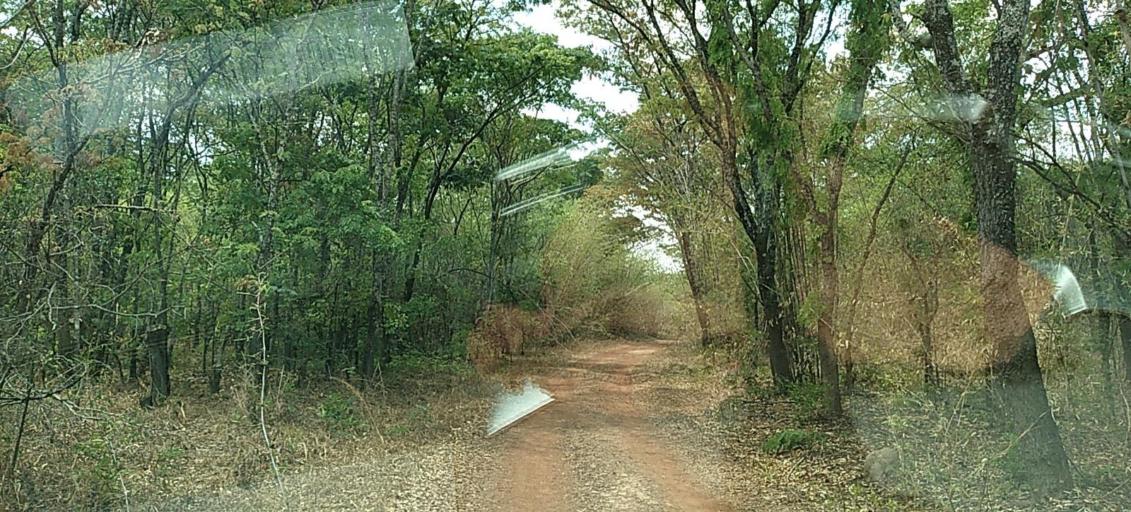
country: ZM
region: Copperbelt
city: Chililabombwe
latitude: -12.4795
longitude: 27.6446
